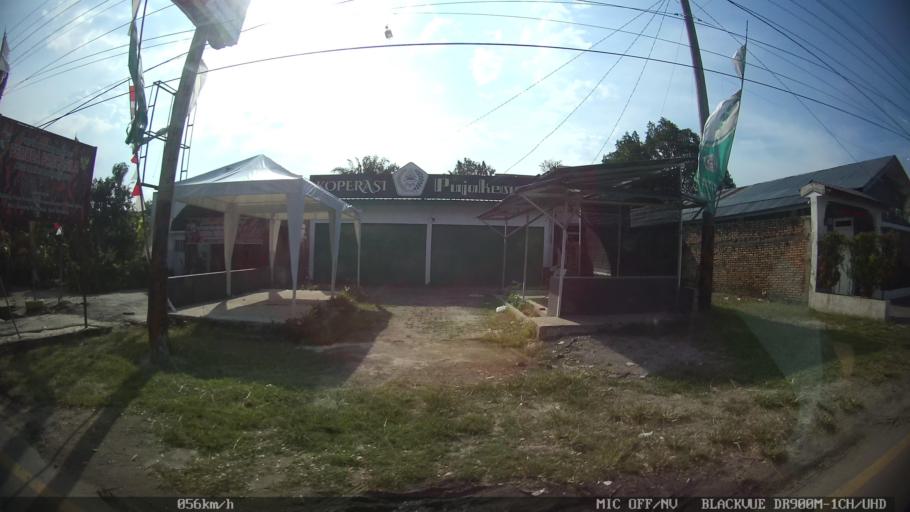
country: ID
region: North Sumatra
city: Percut
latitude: 3.5911
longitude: 98.8056
